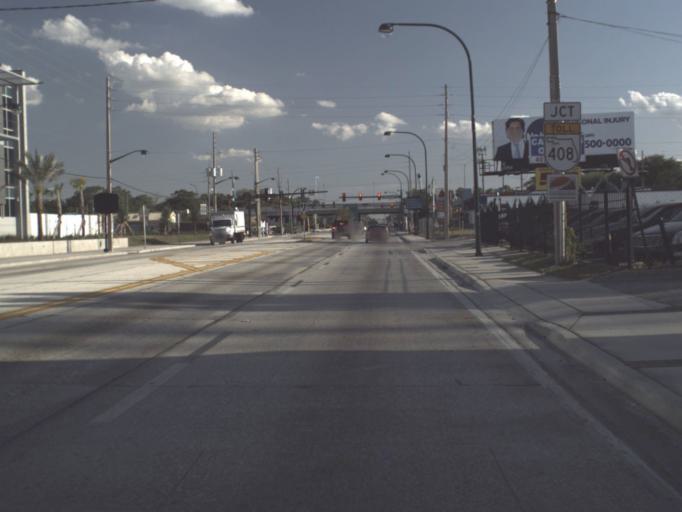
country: US
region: Florida
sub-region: Orange County
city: Orlando
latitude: 28.5380
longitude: -81.3973
